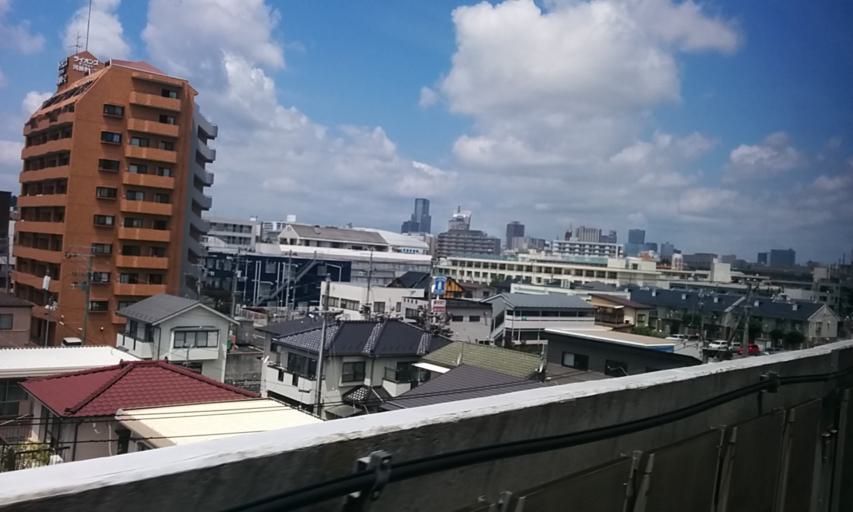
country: JP
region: Miyagi
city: Sendai
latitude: 38.2392
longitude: 140.8942
